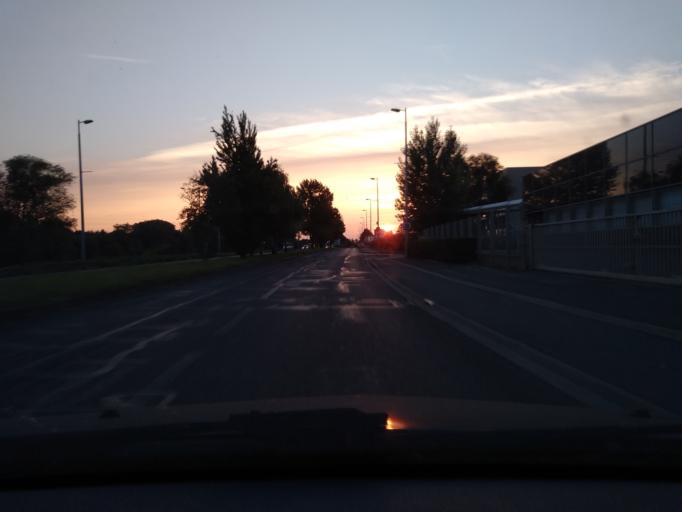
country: FR
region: Centre
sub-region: Departement d'Indre-et-Loire
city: Tours
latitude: 47.3740
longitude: 0.6763
